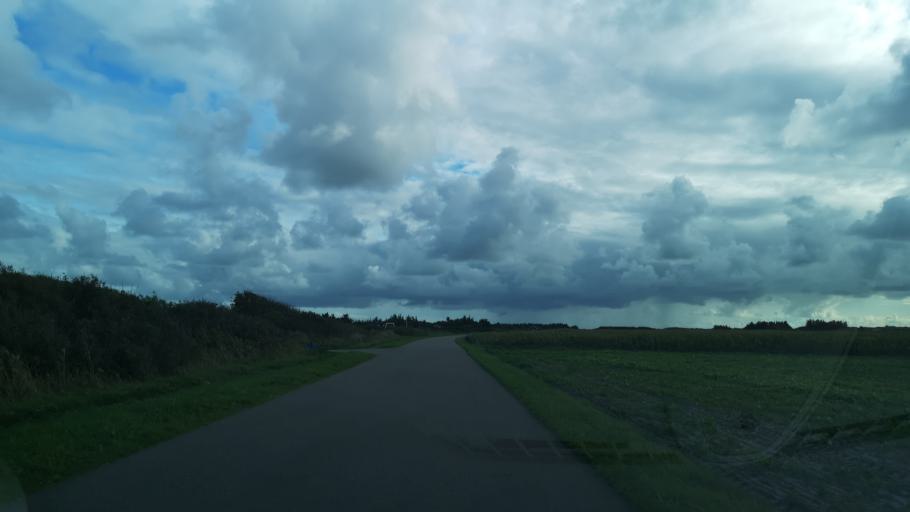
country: DK
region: Central Jutland
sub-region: Ringkobing-Skjern Kommune
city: Ringkobing
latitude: 56.1366
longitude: 8.1333
